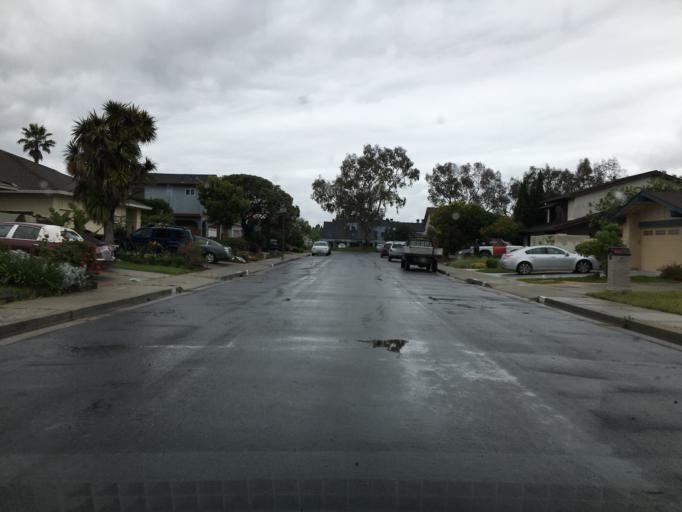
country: US
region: California
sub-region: San Mateo County
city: Redwood Shores
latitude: 37.5334
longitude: -122.2444
